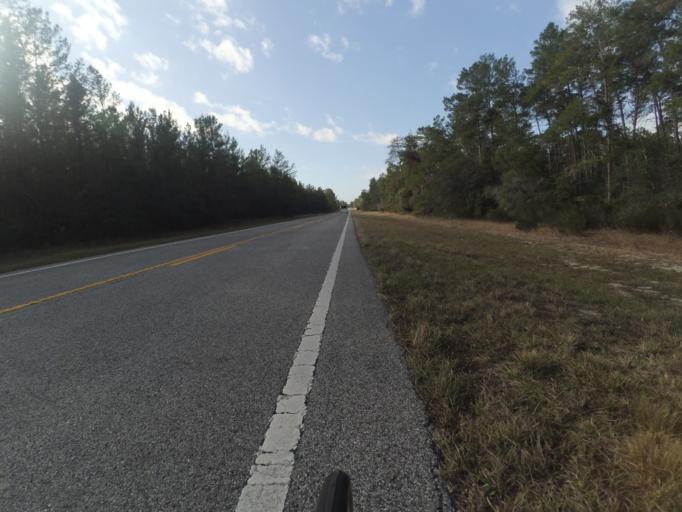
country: US
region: Florida
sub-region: Lake County
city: Astor
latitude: 29.1250
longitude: -81.6114
